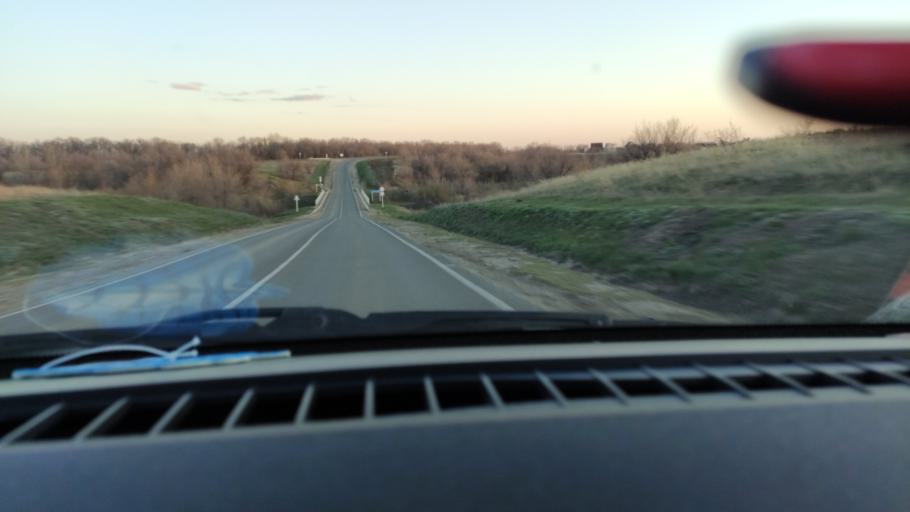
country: RU
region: Saratov
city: Privolzhskiy
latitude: 51.3449
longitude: 46.0434
